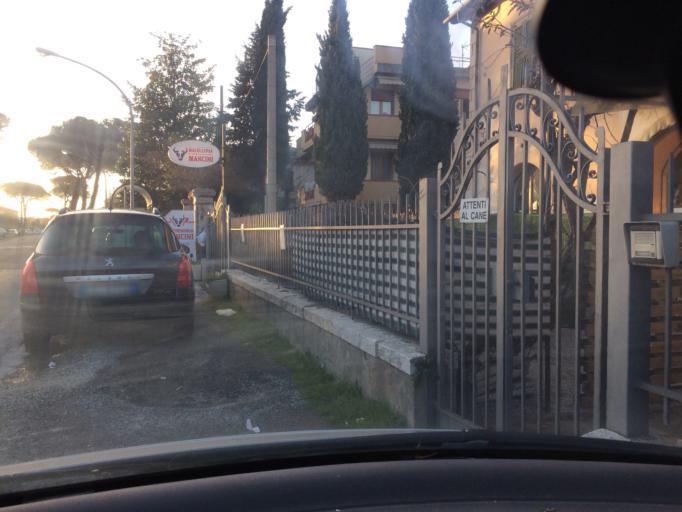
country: IT
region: Tuscany
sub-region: Province of Pisa
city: Gello
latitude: 43.7220
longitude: 10.4408
